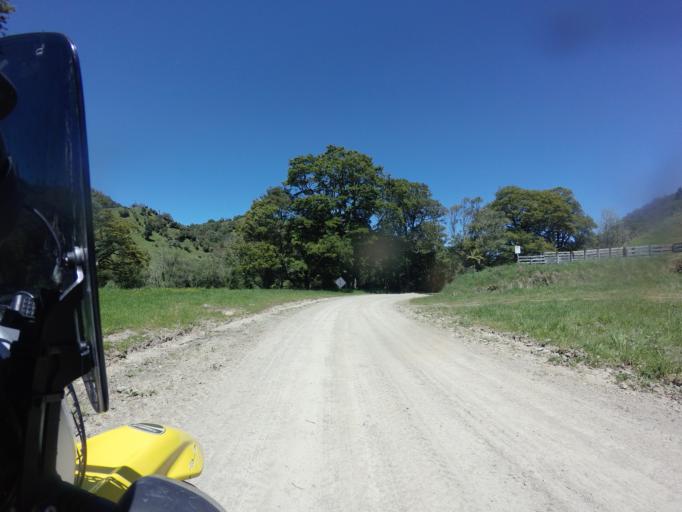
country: NZ
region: Bay of Plenty
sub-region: Opotiki District
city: Opotiki
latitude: -38.4140
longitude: 177.4082
